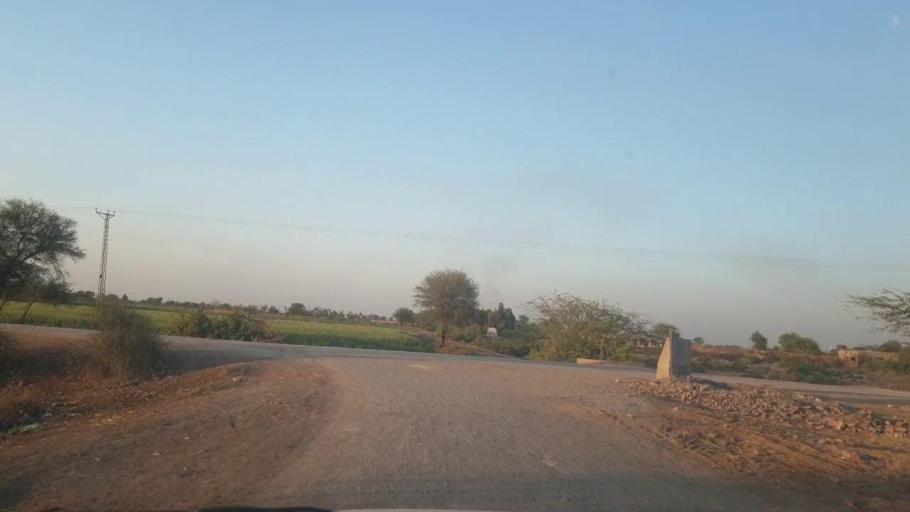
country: PK
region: Sindh
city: Mirpur Khas
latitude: 25.4692
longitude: 69.0701
